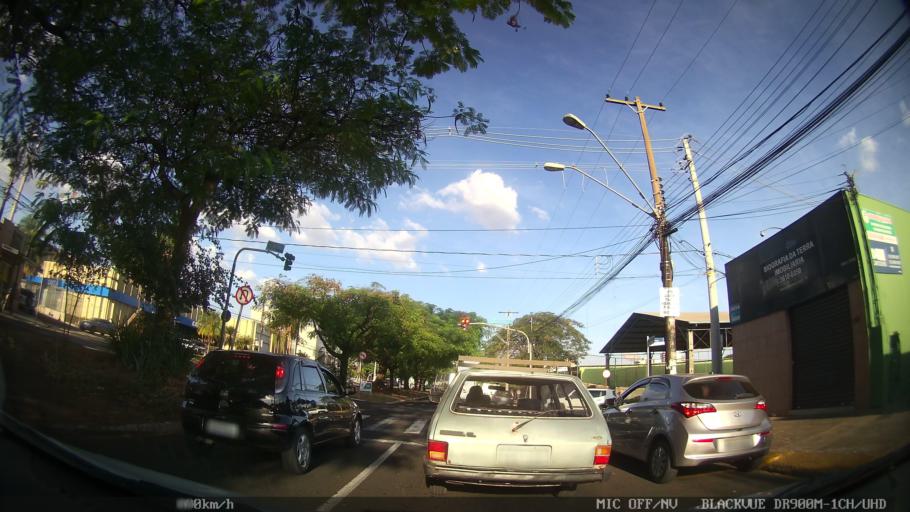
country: BR
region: Sao Paulo
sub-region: Ribeirao Preto
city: Ribeirao Preto
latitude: -21.1754
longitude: -47.7931
